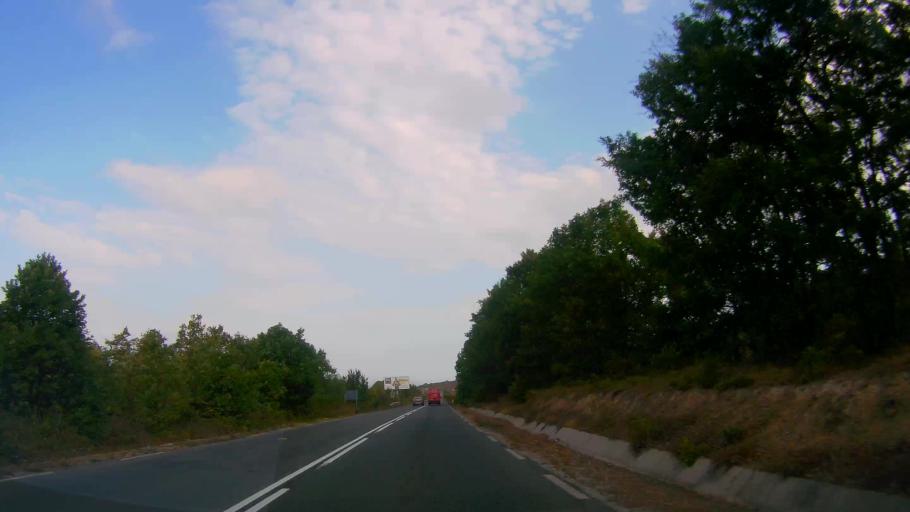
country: BG
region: Burgas
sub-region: Obshtina Sozopol
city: Sozopol
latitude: 42.3711
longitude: 27.6833
